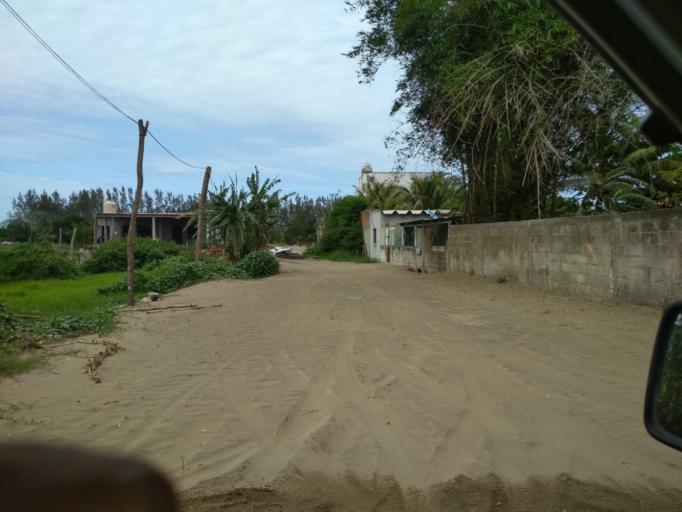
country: MX
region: Veracruz
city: Anton Lizardo
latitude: 19.0359
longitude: -95.9704
